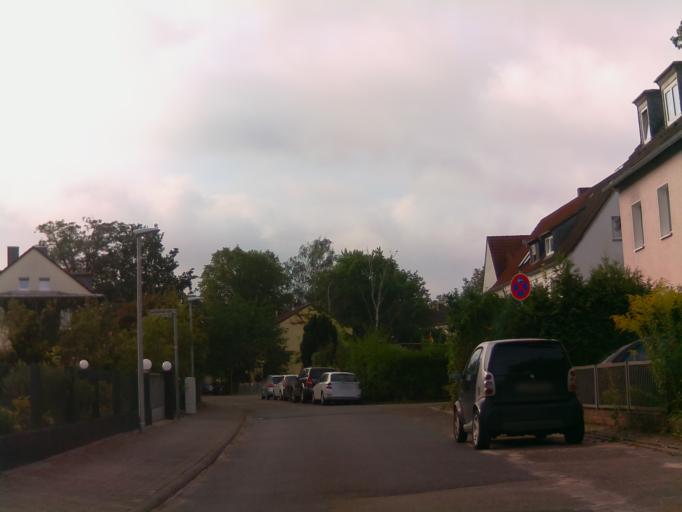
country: DE
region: Hesse
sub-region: Regierungsbezirk Darmstadt
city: Hanau am Main
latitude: 50.1408
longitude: 8.9416
